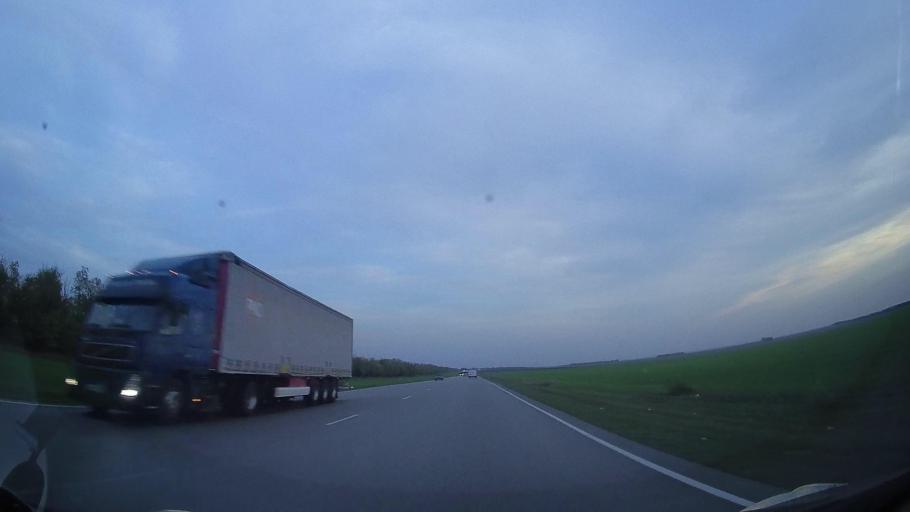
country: RU
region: Rostov
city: Kagal'nitskaya
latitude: 46.9114
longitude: 40.1132
